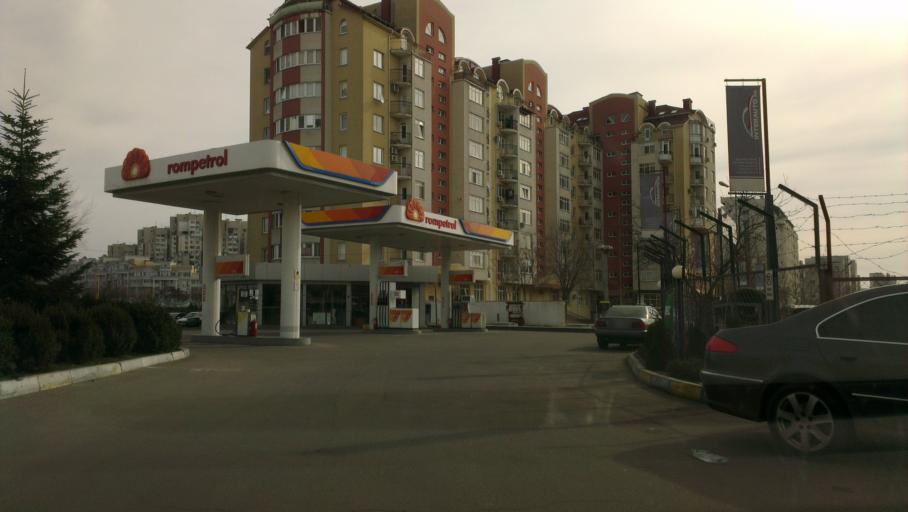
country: MD
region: Chisinau
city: Chisinau
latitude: 47.0377
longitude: 28.8251
